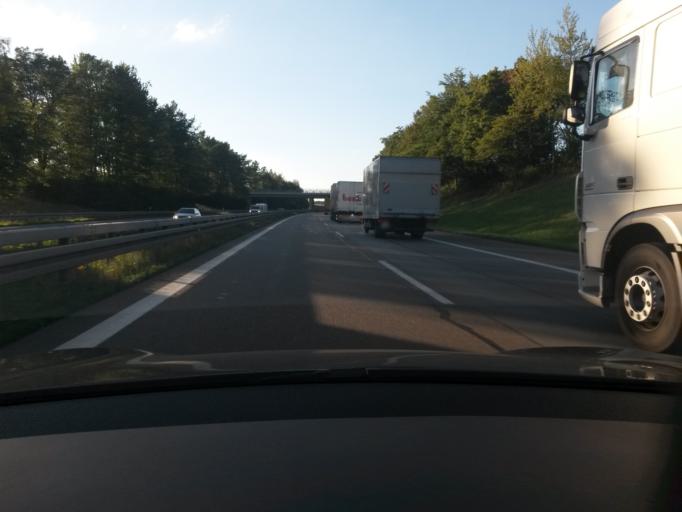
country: DE
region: Bavaria
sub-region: Upper Palatinate
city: Brunn
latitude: 49.0717
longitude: 11.9097
